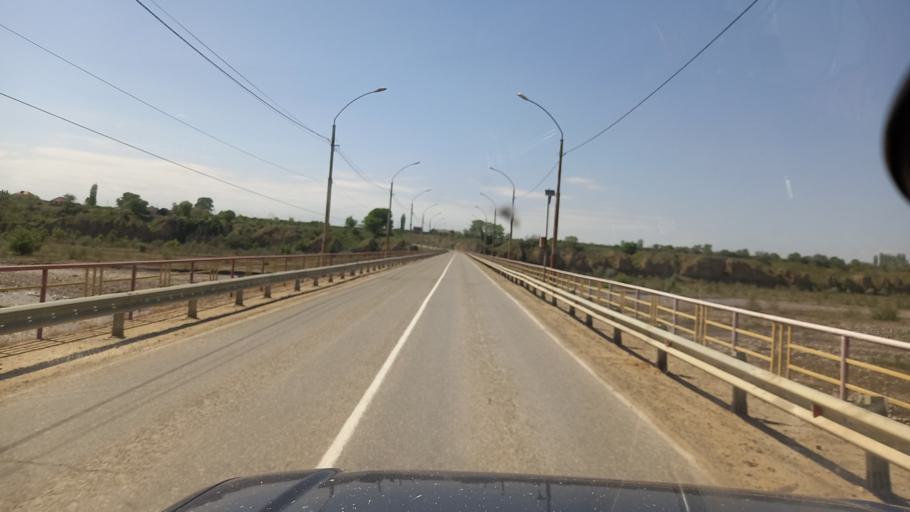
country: RU
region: Dagestan
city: Novaya Maka
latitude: 41.7365
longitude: 48.4493
